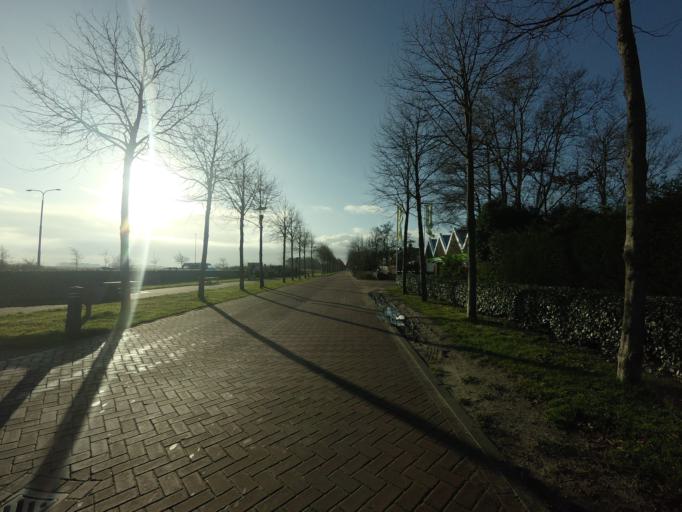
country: NL
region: North Holland
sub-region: Gemeente Texel
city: Den Burg
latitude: 53.1547
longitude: 4.8696
